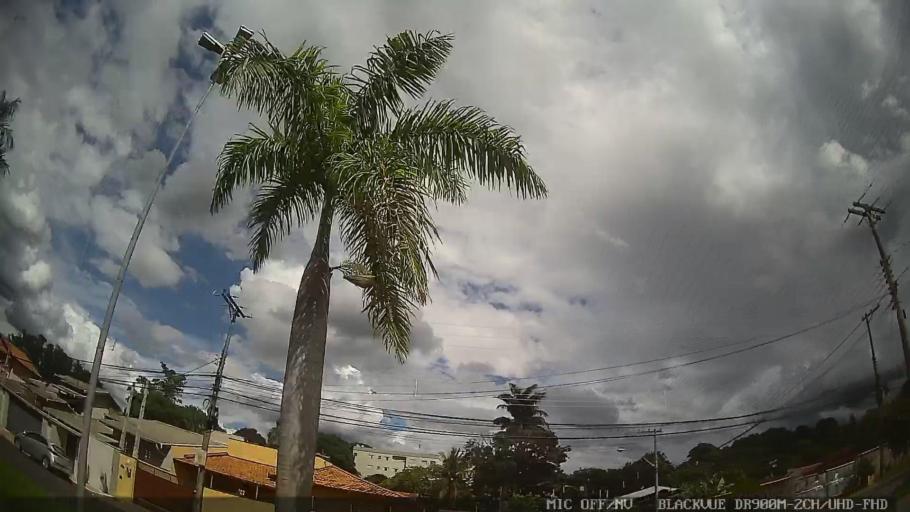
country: BR
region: Sao Paulo
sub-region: Jaguariuna
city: Jaguariuna
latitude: -22.6818
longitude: -46.9757
